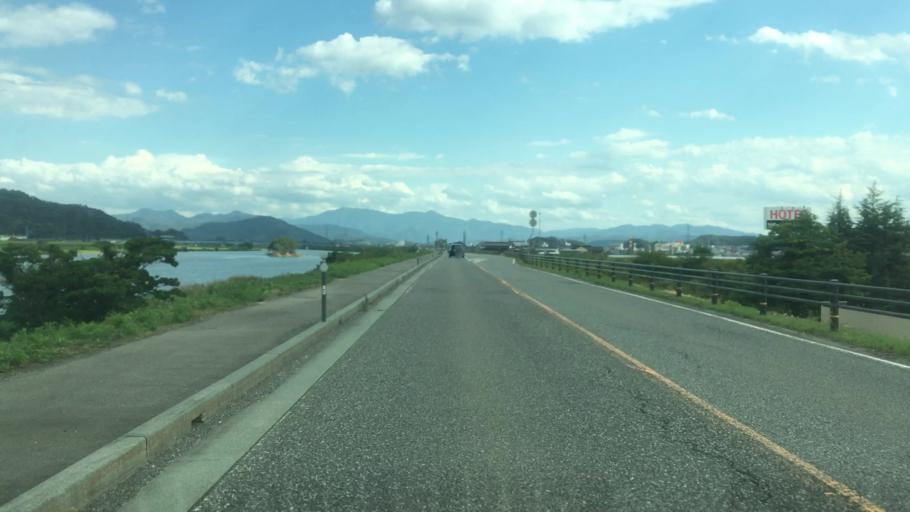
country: JP
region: Hyogo
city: Toyooka
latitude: 35.5696
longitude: 134.8091
